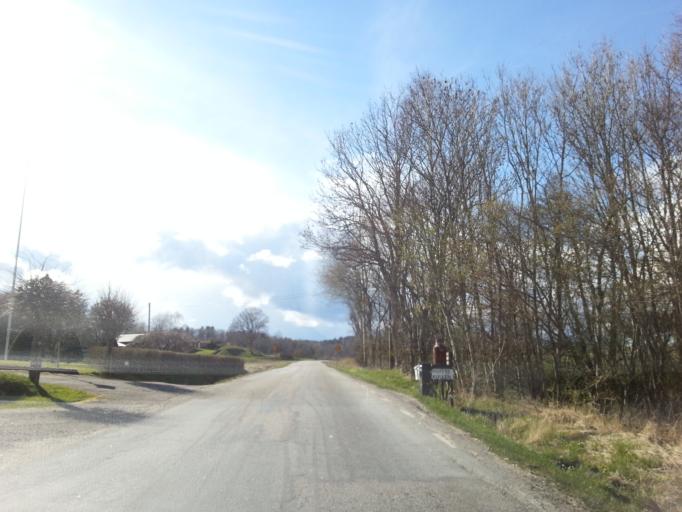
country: SE
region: Vaestra Goetaland
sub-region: Ale Kommun
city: Nodinge-Nol
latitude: 57.9255
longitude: 12.0499
